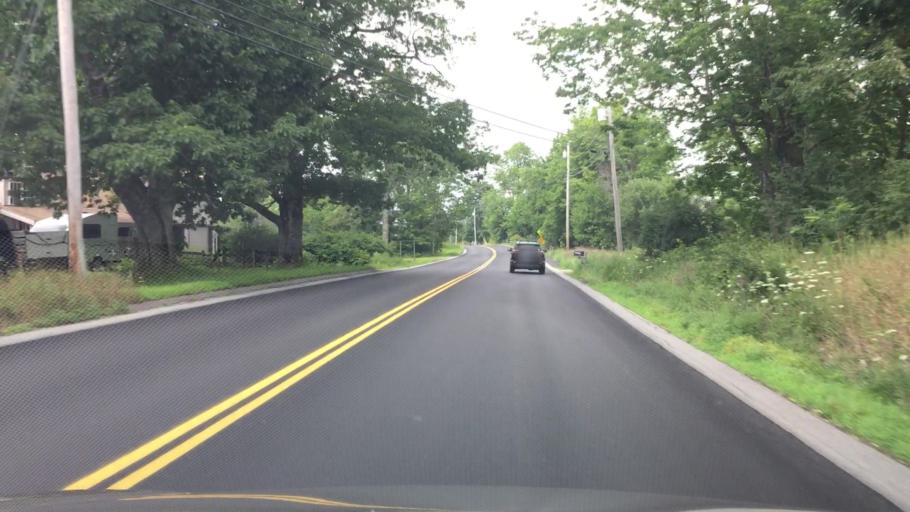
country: US
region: Maine
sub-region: Waldo County
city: Winterport
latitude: 44.6260
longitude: -68.8330
